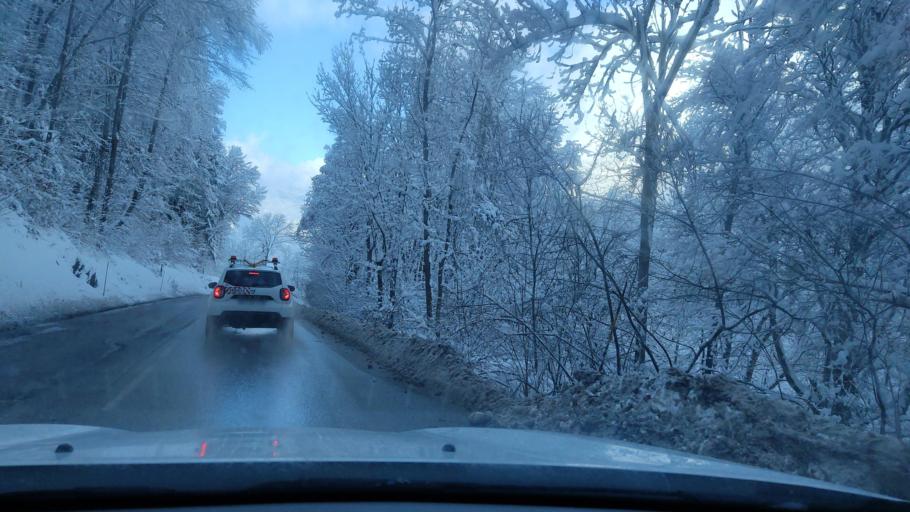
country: FR
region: Rhone-Alpes
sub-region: Departement de la Savoie
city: Saint-Bon-Tarentaise
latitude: 45.4412
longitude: 6.6209
